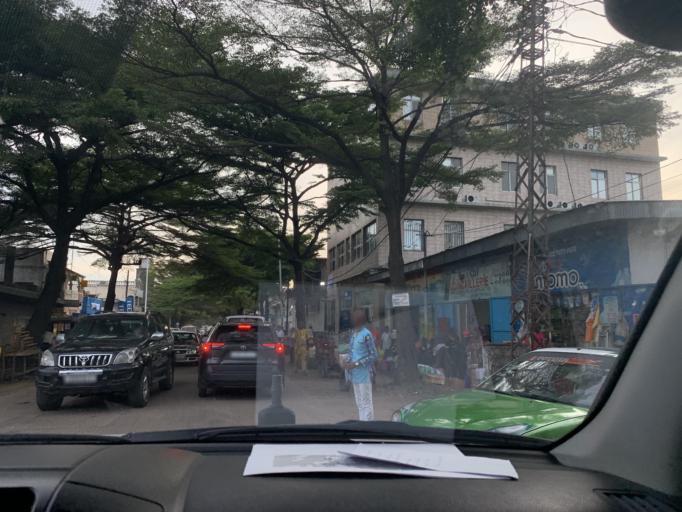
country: CG
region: Brazzaville
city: Brazzaville
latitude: -4.2658
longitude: 15.2861
